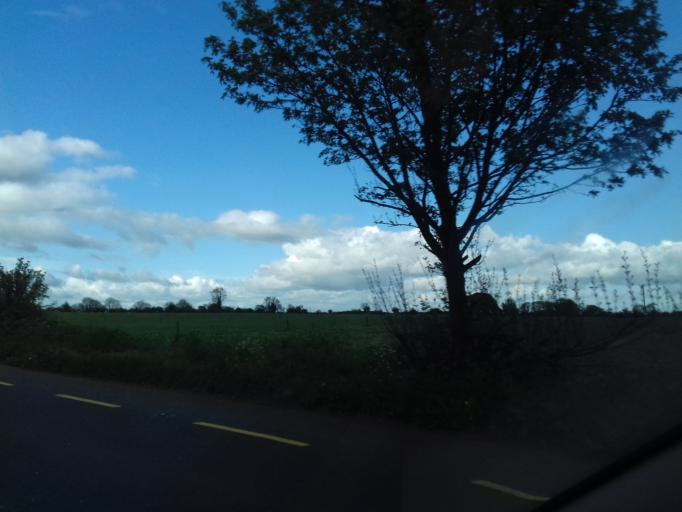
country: IE
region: Leinster
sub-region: Kilkenny
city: Kilkenny
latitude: 52.5970
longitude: -7.2417
